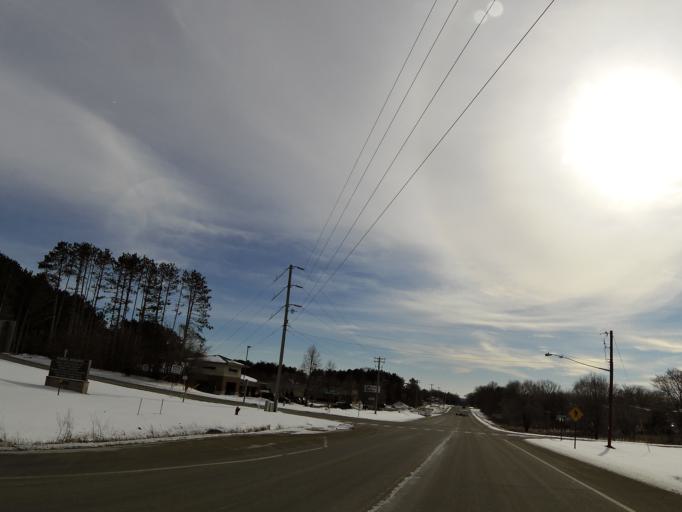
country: US
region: Wisconsin
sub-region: Saint Croix County
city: North Hudson
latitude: 45.0064
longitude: -92.7530
